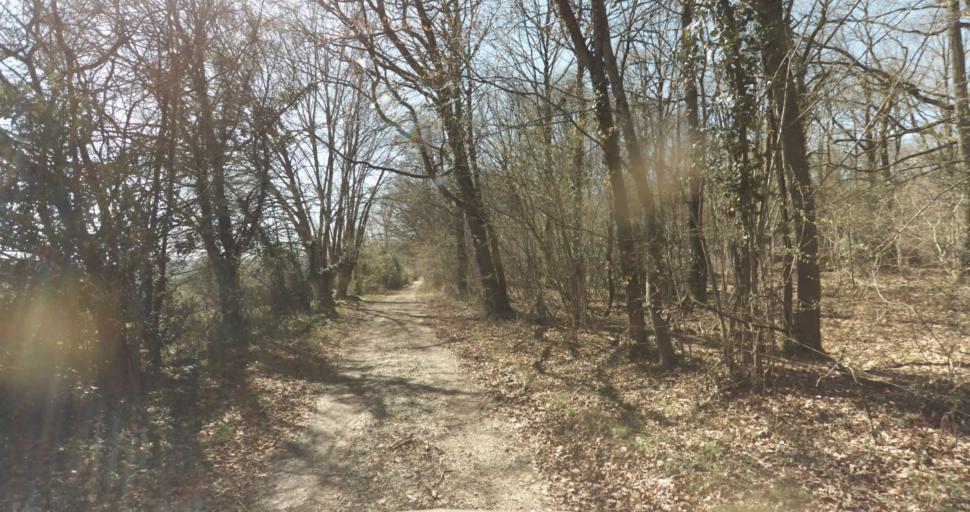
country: FR
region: Lower Normandy
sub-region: Departement du Calvados
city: Livarot
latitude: 48.9359
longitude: 0.0806
